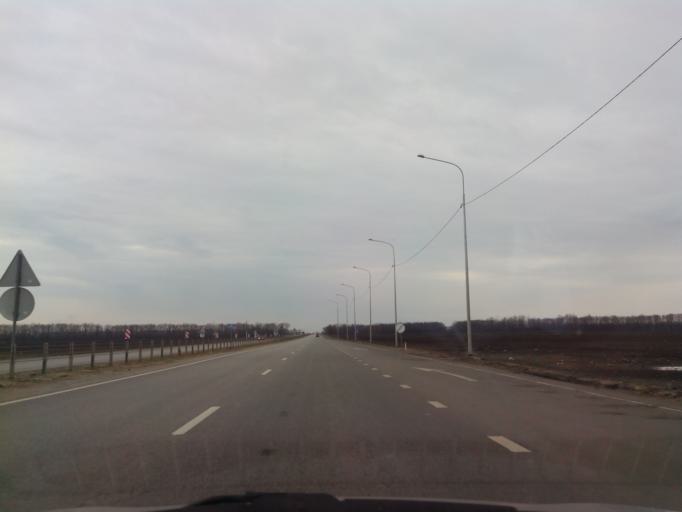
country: RU
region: Tambov
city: Zavoronezhskoye
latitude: 52.8921
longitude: 40.6937
